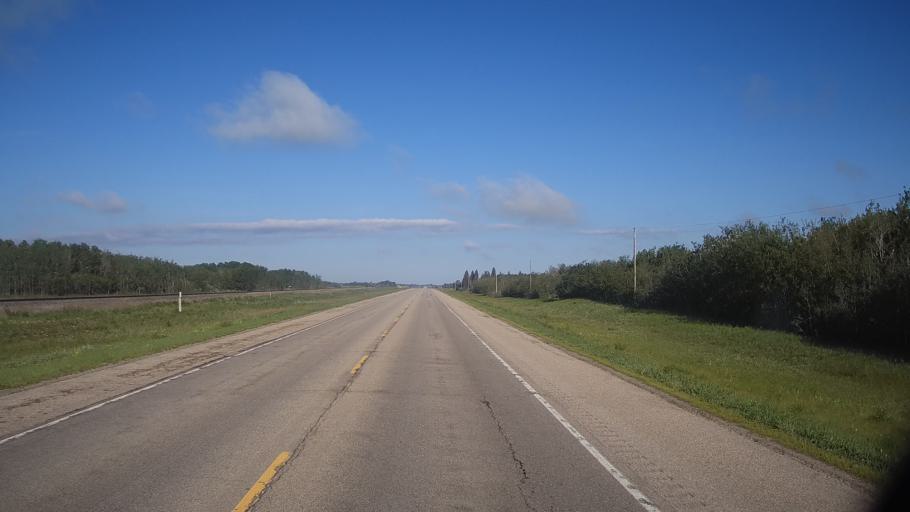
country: CA
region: Saskatchewan
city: Lanigan
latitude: 51.8559
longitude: -105.0906
